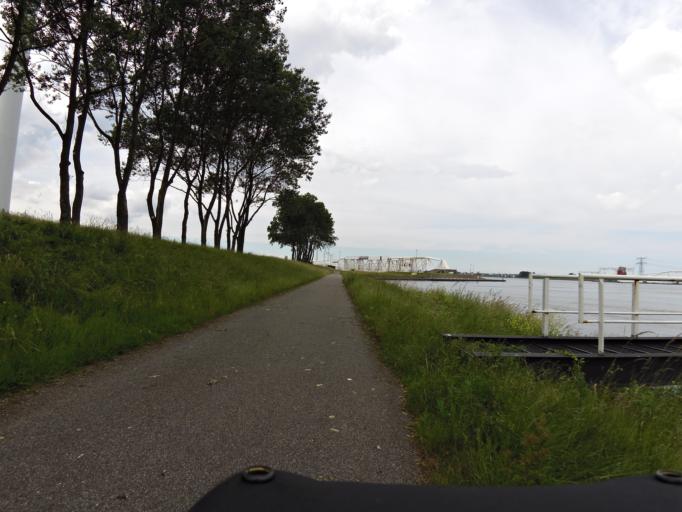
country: NL
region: South Holland
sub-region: Gemeente Rotterdam
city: Hoek van Holland
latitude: 51.9499
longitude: 4.1659
